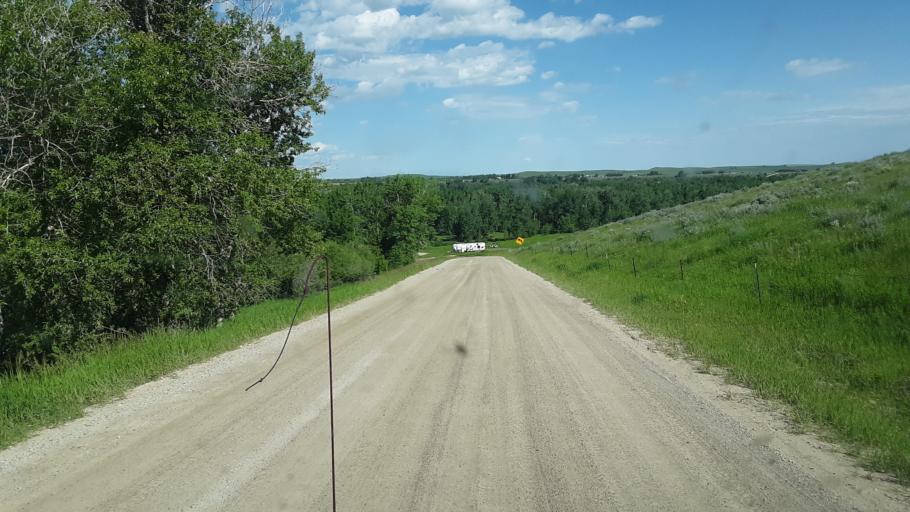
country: US
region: Montana
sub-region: Carbon County
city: Red Lodge
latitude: 45.2786
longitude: -109.2033
